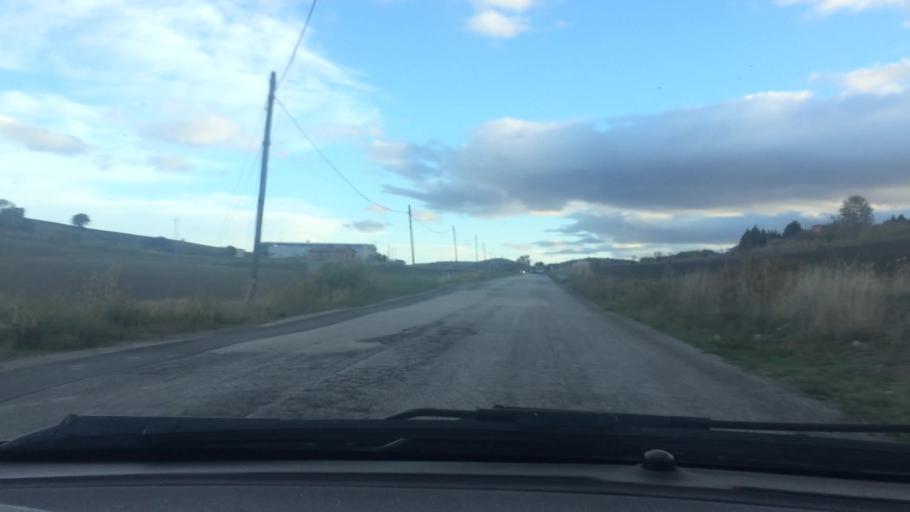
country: IT
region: Basilicate
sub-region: Provincia di Potenza
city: Tolve
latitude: 40.7078
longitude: 16.0169
